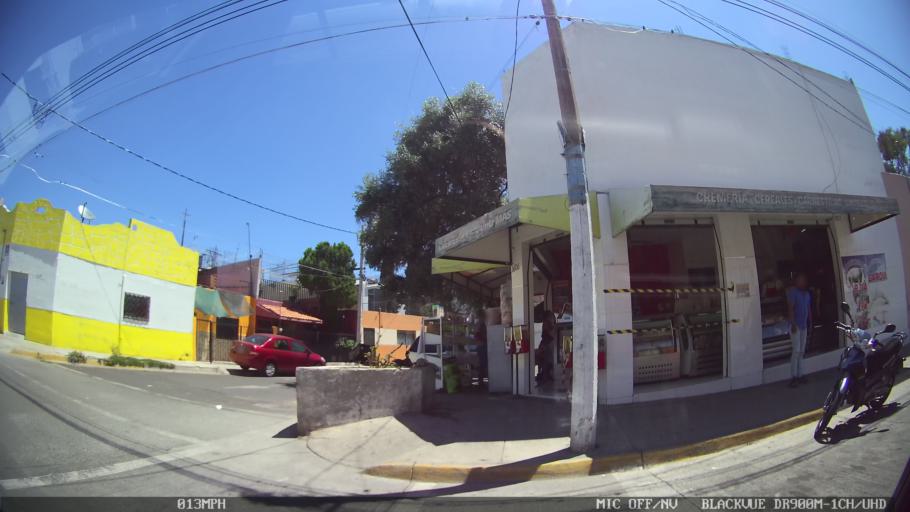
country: MX
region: Jalisco
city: Tlaquepaque
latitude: 20.6856
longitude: -103.2912
